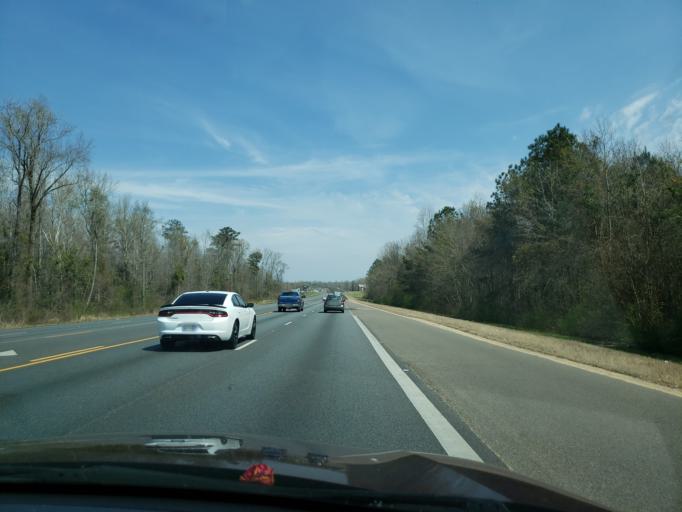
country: US
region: Alabama
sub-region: Elmore County
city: Millbrook
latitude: 32.5004
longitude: -86.3939
